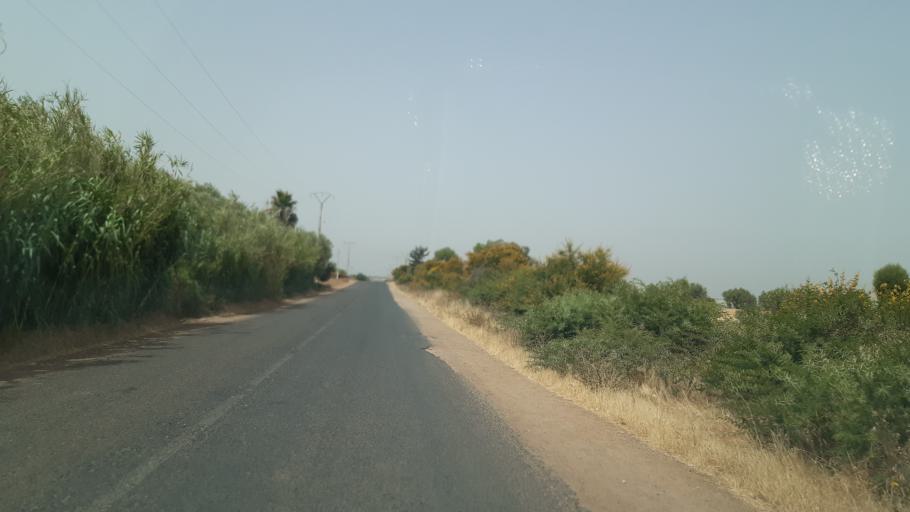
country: MA
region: Fes-Boulemane
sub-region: Fes
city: Oulad Tayeb
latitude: 33.8258
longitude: -5.1634
